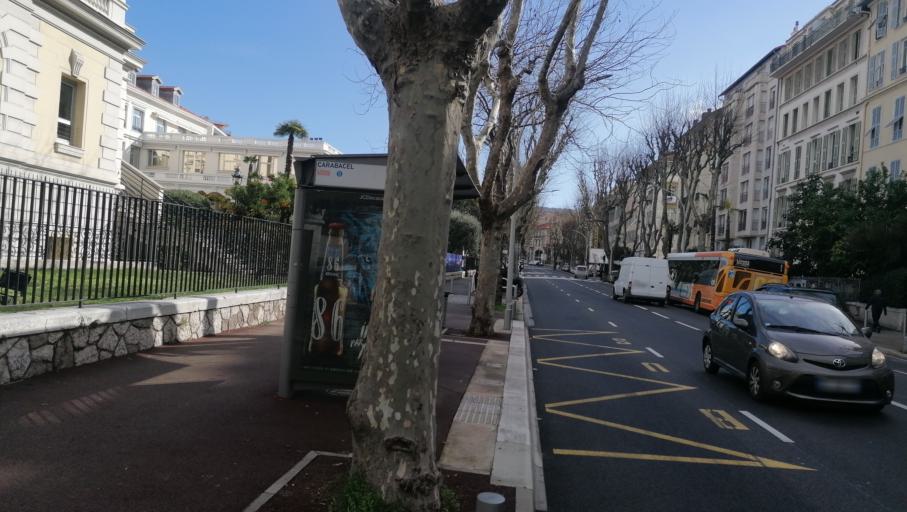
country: FR
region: Provence-Alpes-Cote d'Azur
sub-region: Departement des Alpes-Maritimes
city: Nice
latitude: 43.7040
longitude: 7.2747
